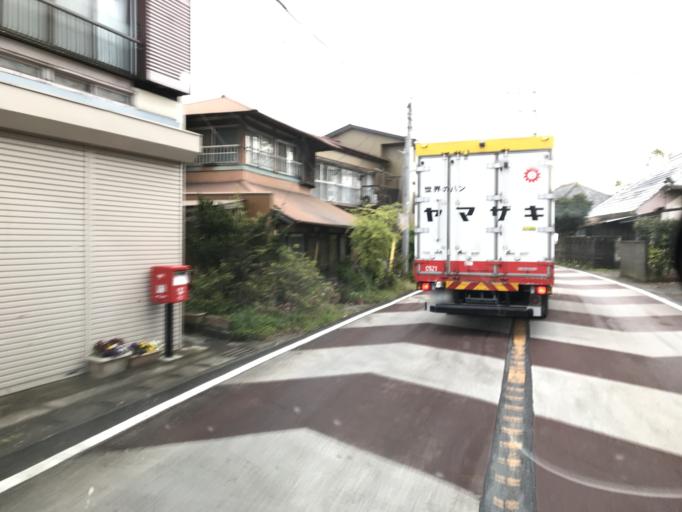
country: JP
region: Chiba
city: Yokaichiba
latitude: 35.7488
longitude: 140.5594
